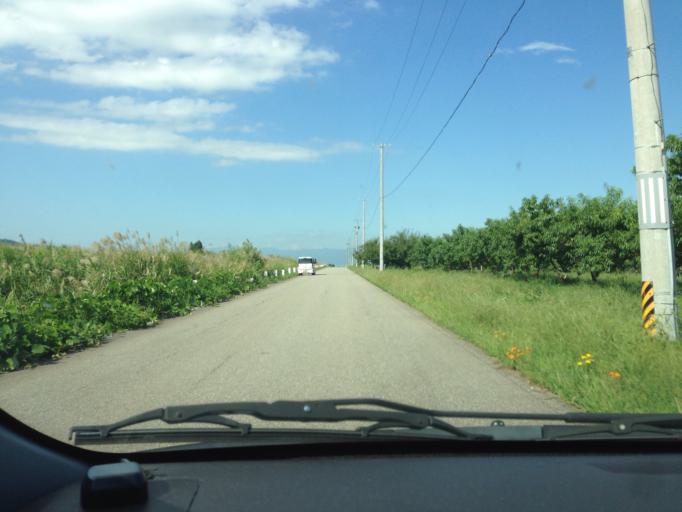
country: JP
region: Fukushima
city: Kitakata
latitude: 37.4348
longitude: 139.8081
